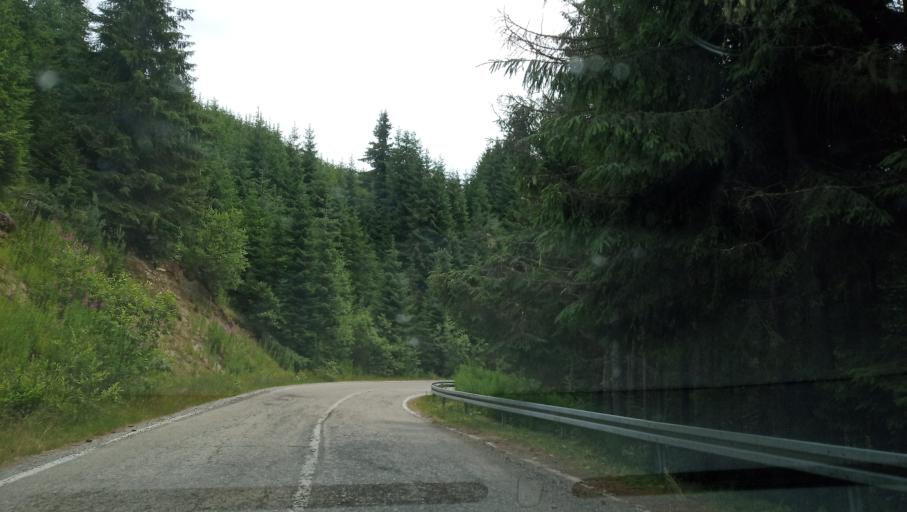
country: RO
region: Valcea
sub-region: Comuna Voineasa
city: Voineasa
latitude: 45.4194
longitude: 23.7401
